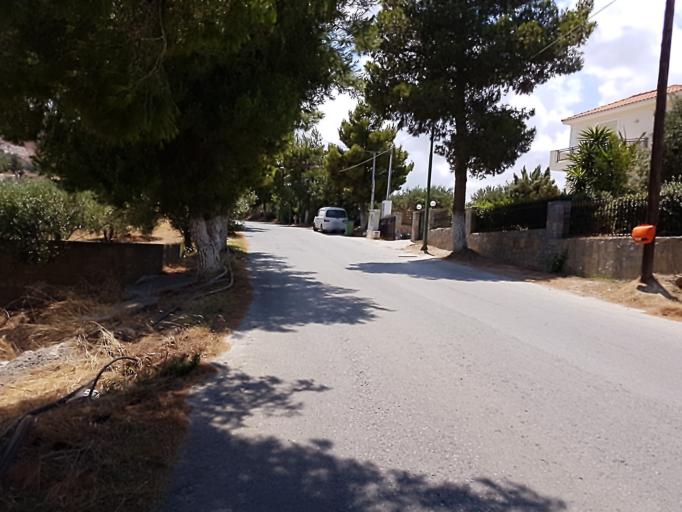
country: GR
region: Crete
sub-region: Nomos Irakleiou
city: Limin Khersonisou
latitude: 35.3115
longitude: 25.3762
